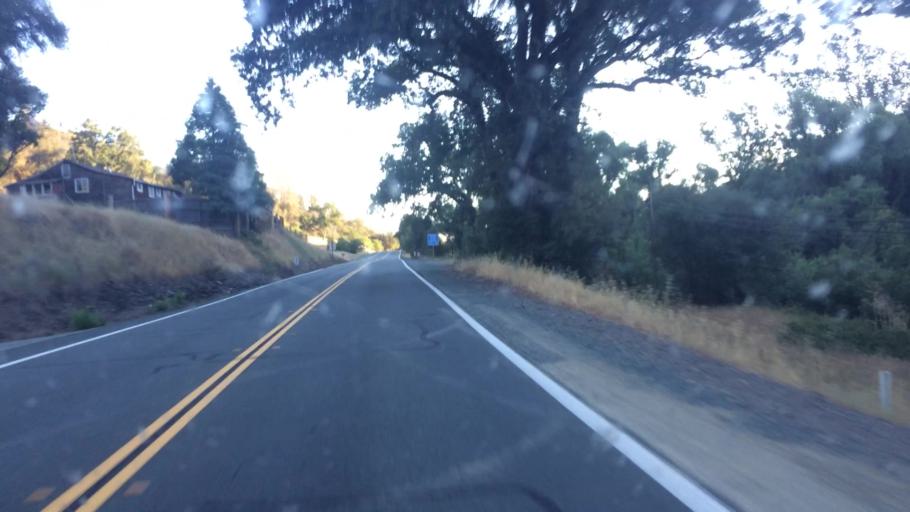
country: US
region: California
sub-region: Amador County
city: Plymouth
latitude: 38.5342
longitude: -120.8475
